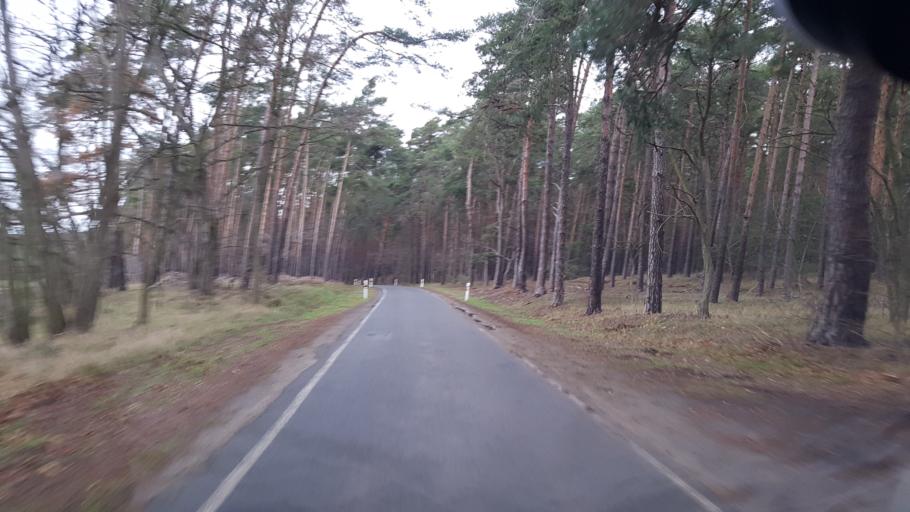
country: DE
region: Brandenburg
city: Hohenbucko
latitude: 51.7400
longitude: 13.4738
